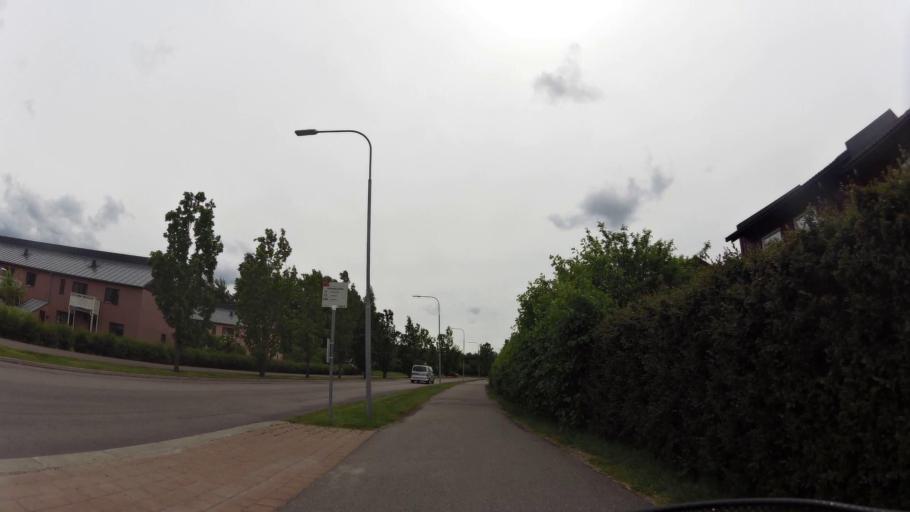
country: SE
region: OEstergoetland
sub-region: Linkopings Kommun
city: Linkoping
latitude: 58.3883
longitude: 15.5741
